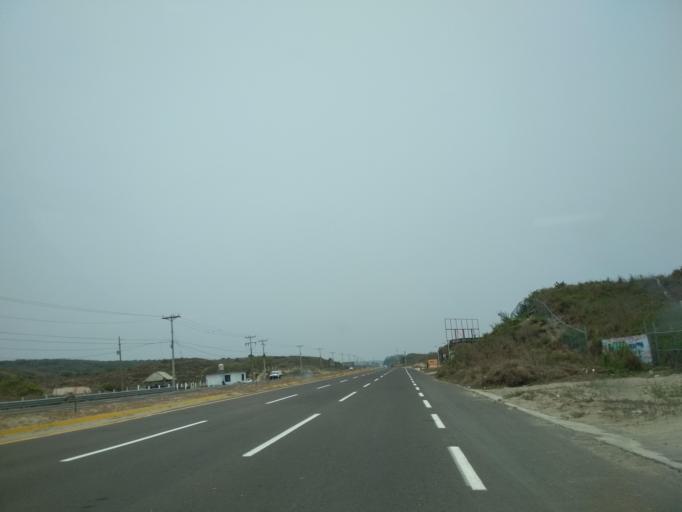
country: MX
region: Veracruz
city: Anton Lizardo
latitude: 19.0536
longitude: -96.0312
